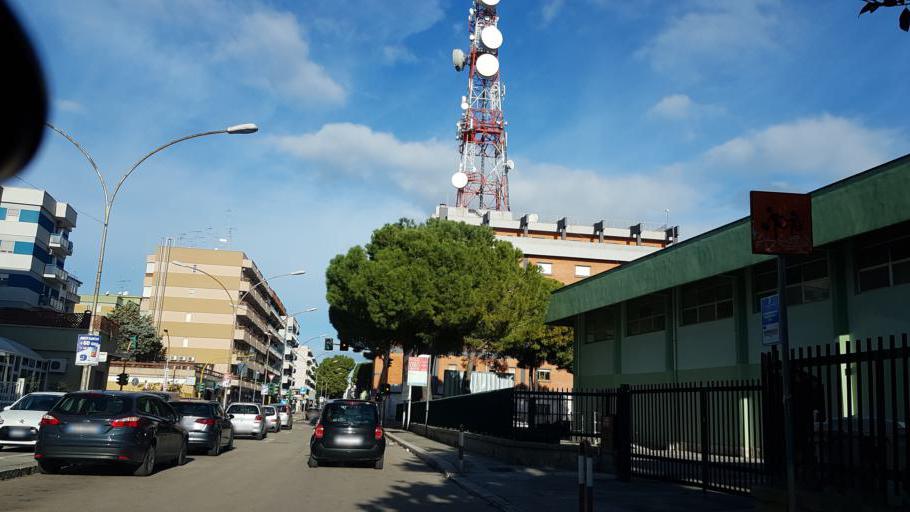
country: IT
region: Apulia
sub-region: Provincia di Brindisi
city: Brindisi
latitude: 40.6255
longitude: 17.9287
